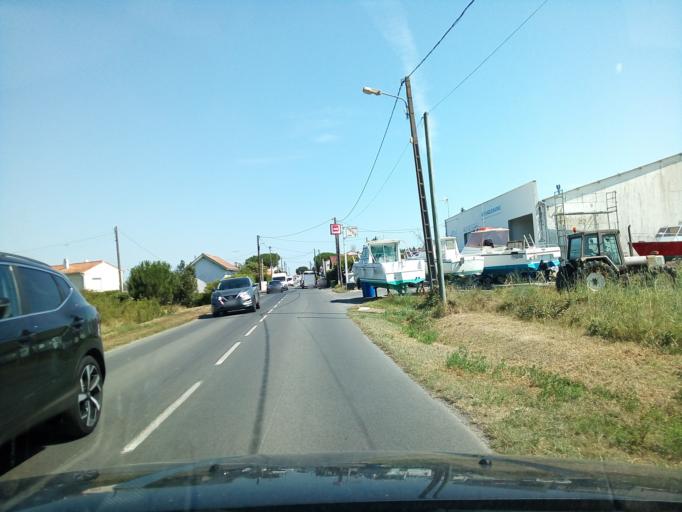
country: FR
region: Poitou-Charentes
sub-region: Departement de la Charente-Maritime
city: Boyard-Ville
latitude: 45.9667
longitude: -1.2475
